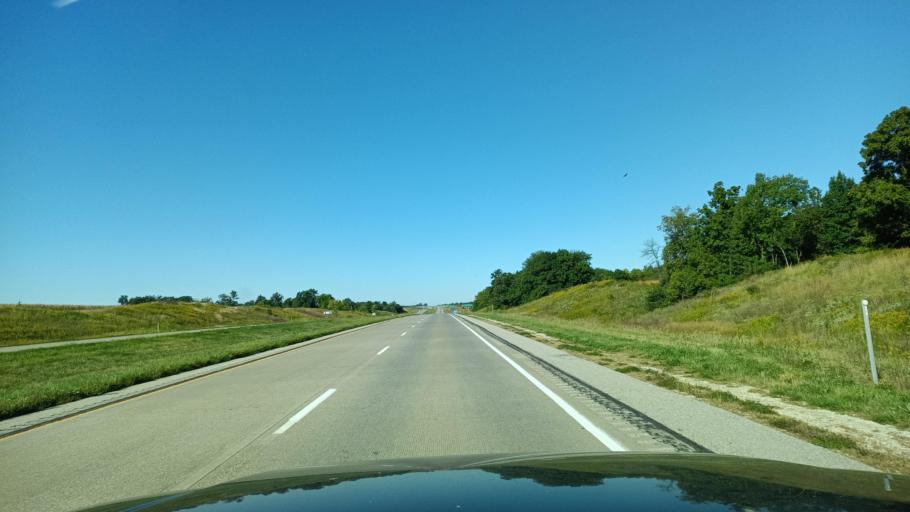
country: US
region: Iowa
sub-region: Lee County
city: Fort Madison
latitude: 40.6707
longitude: -91.3061
